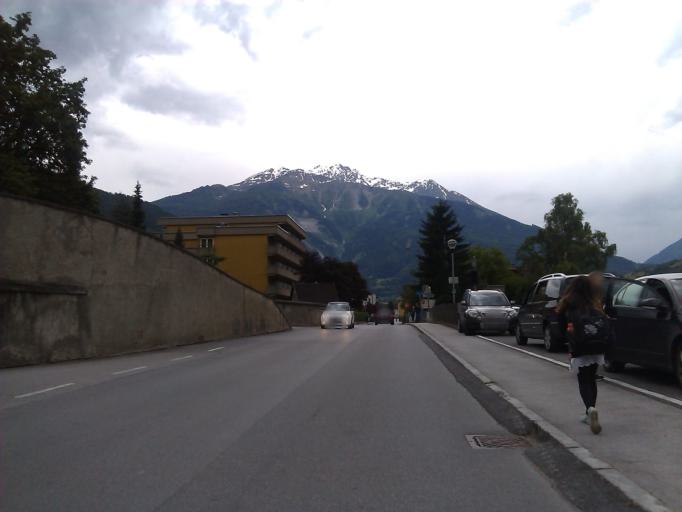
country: AT
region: Tyrol
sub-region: Politischer Bezirk Landeck
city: Zams
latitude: 47.1631
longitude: 10.5906
